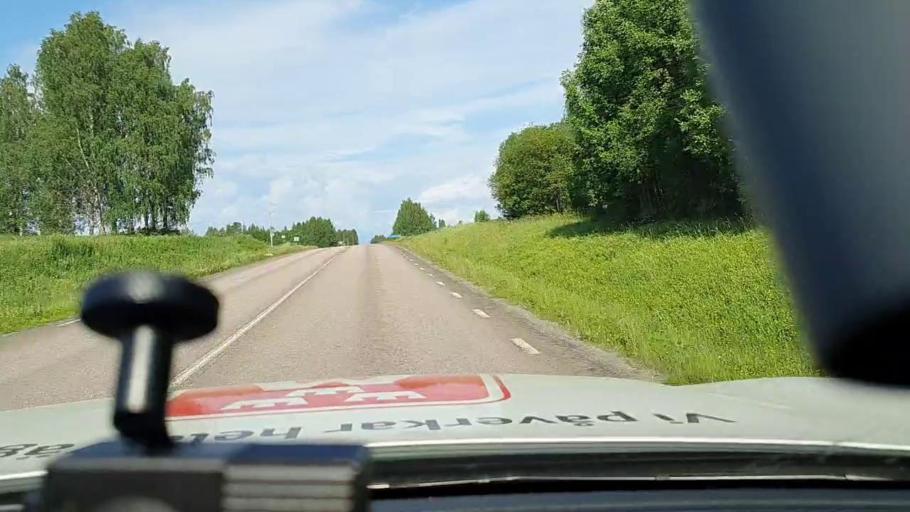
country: SE
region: Norrbotten
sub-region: Alvsbyns Kommun
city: AElvsbyn
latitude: 66.0145
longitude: 21.1641
